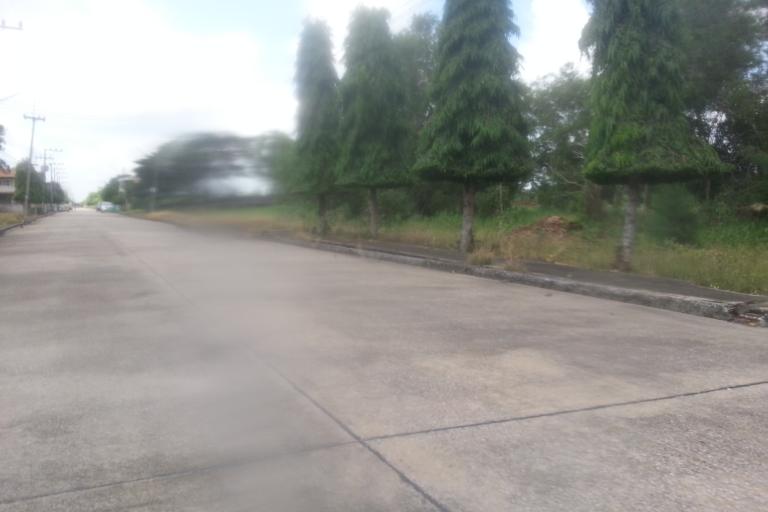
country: TH
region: Pathum Thani
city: Nong Suea
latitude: 14.0609
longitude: 100.8604
